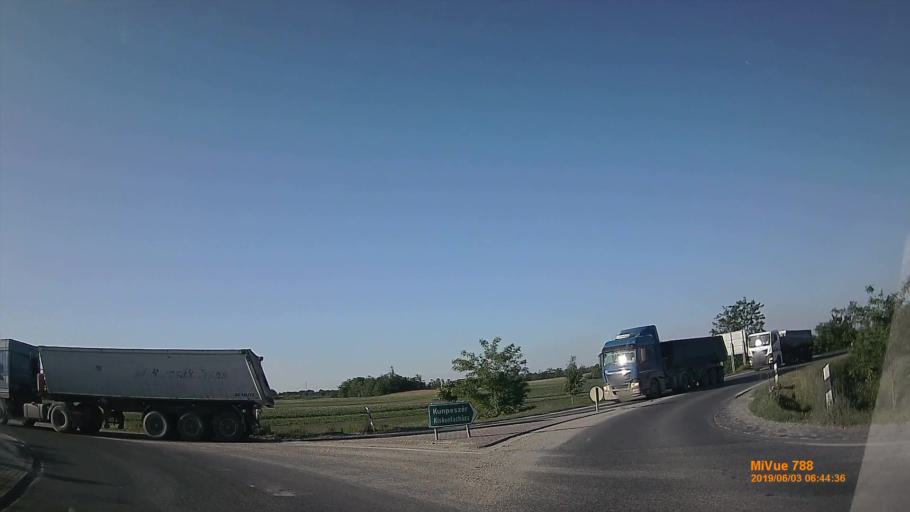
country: HU
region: Pest
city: Bugyi
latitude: 47.2433
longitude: 19.1283
